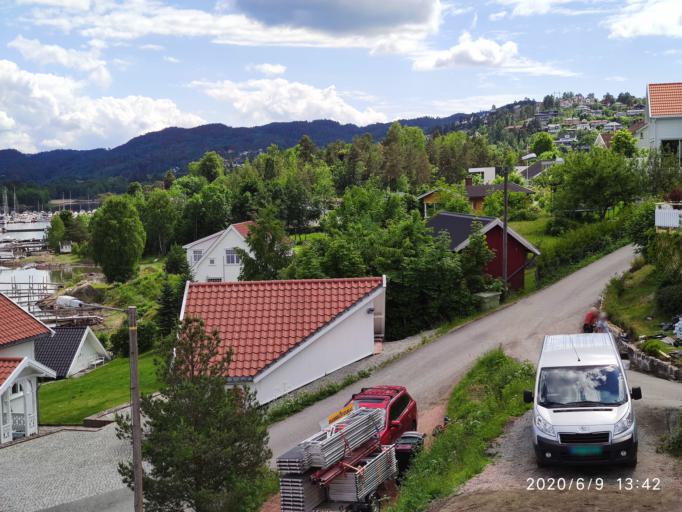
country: NO
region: Buskerud
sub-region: Hurum
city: Saetre
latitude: 59.6865
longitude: 10.5237
